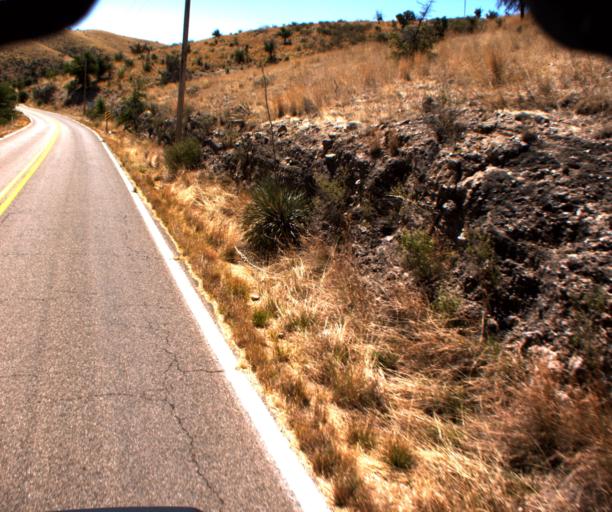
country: US
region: Arizona
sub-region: Santa Cruz County
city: Rio Rico
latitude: 31.3952
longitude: -111.0804
